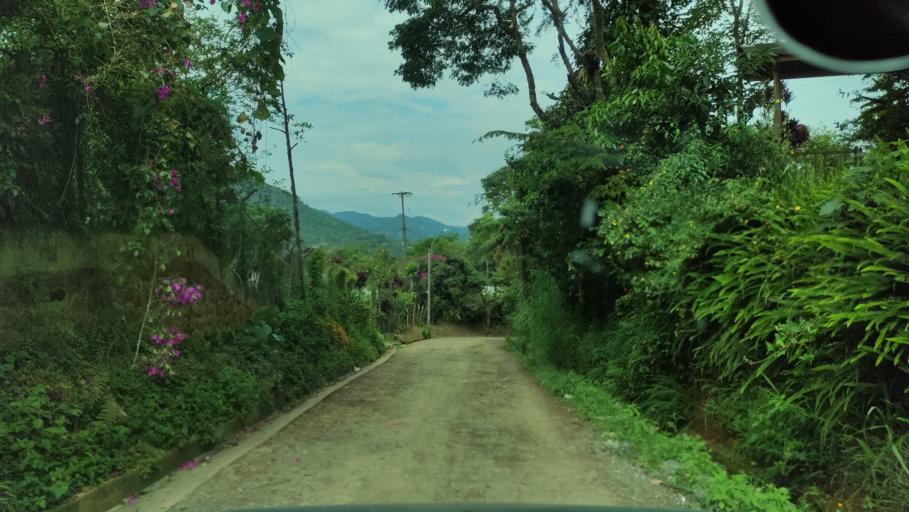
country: CO
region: Valle del Cauca
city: Cali
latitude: 3.4531
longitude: -76.6357
